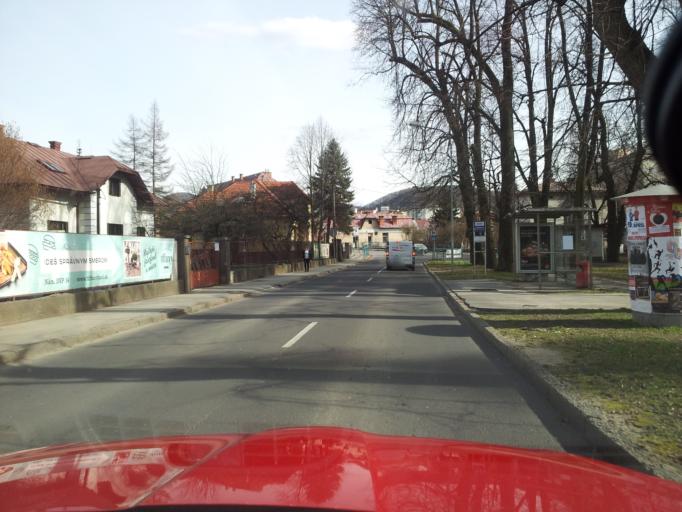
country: SK
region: Banskobystricky
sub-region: Okres Banska Bystrica
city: Banska Bystrica
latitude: 48.7377
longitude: 19.1397
